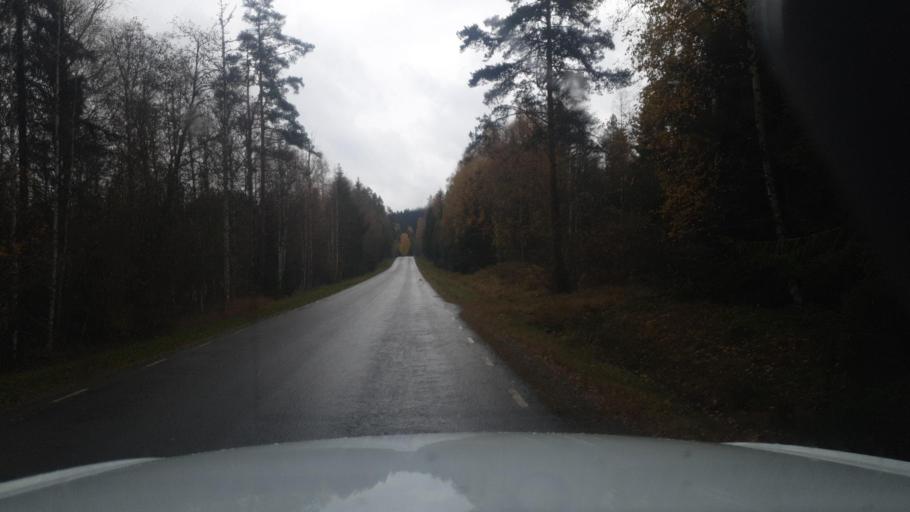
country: SE
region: Vaermland
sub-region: Eda Kommun
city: Charlottenberg
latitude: 60.0180
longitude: 12.6288
